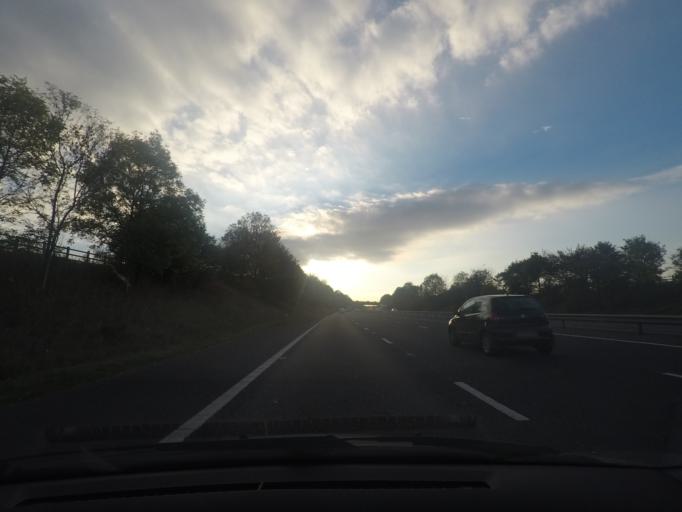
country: GB
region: England
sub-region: North Lincolnshire
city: Scawby
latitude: 53.5511
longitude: -0.5194
